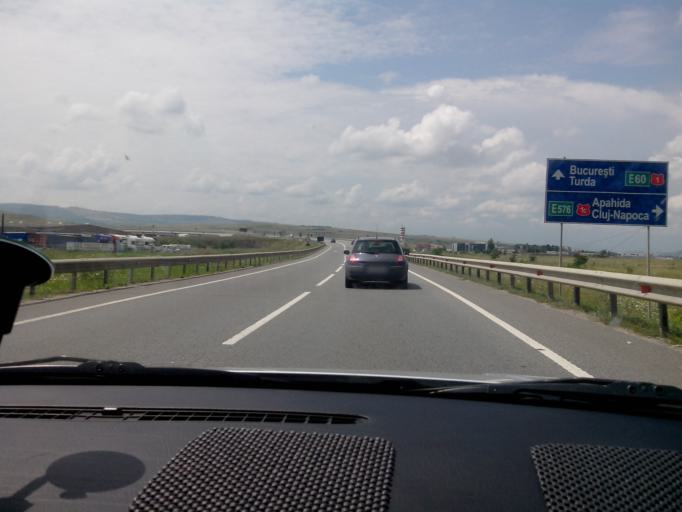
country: RO
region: Cluj
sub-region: Comuna Apahida
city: Sannicoara
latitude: 46.7852
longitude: 23.7084
